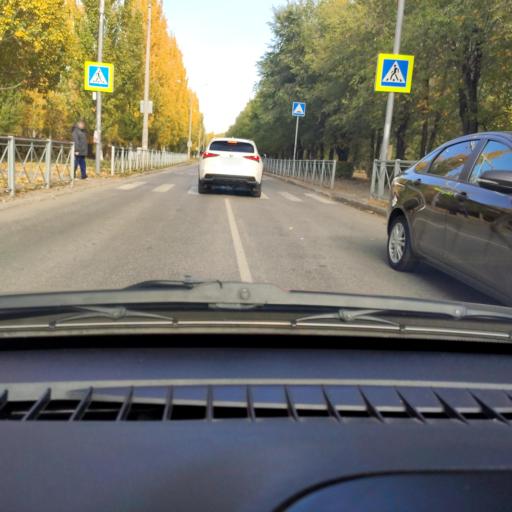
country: RU
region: Samara
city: Tol'yatti
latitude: 53.5301
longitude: 49.2922
